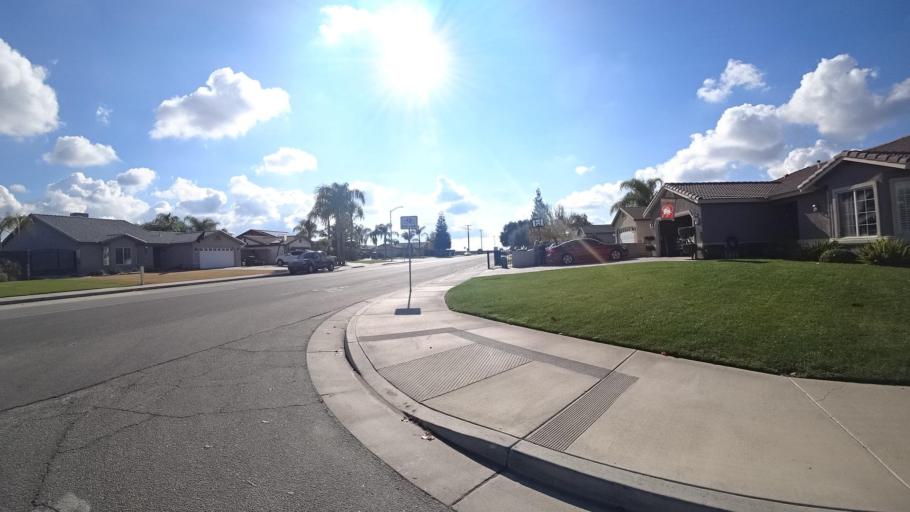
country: US
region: California
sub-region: Kern County
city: McFarland
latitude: 35.6647
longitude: -119.2322
